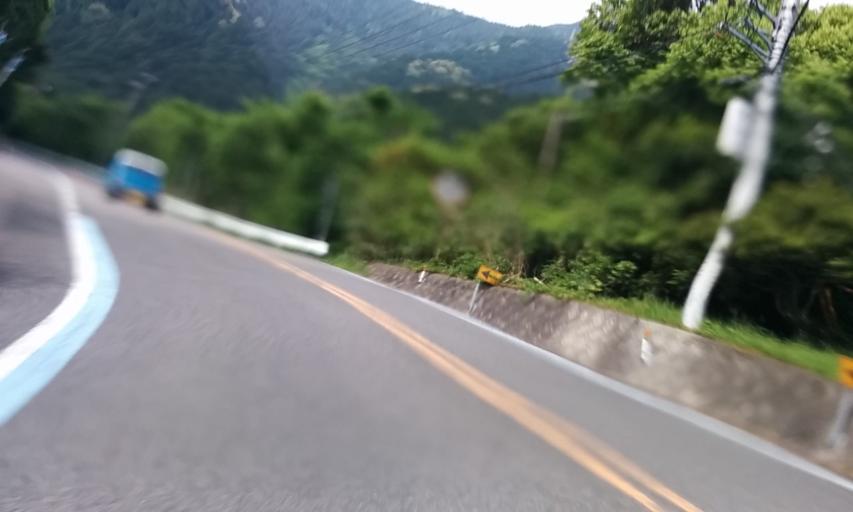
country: JP
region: Ehime
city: Niihama
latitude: 33.9088
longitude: 133.3077
